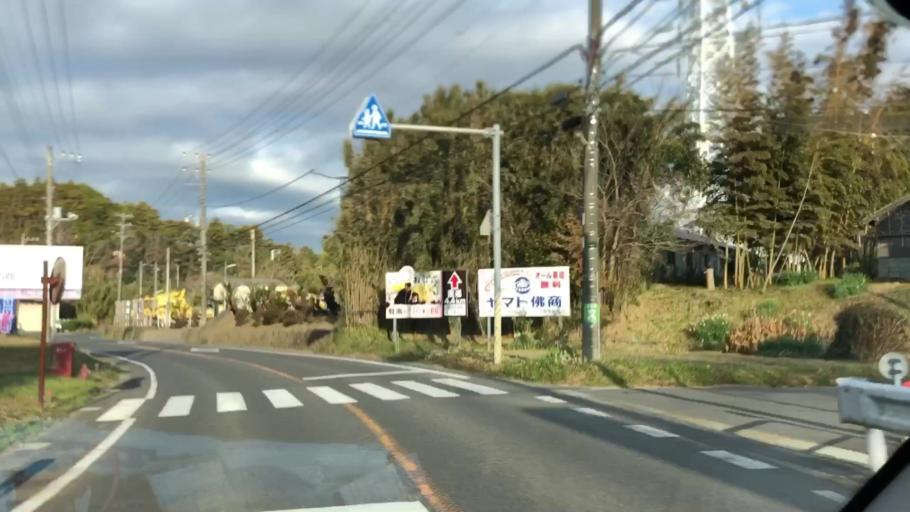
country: JP
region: Chiba
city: Tateyama
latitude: 34.9846
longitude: 139.9438
